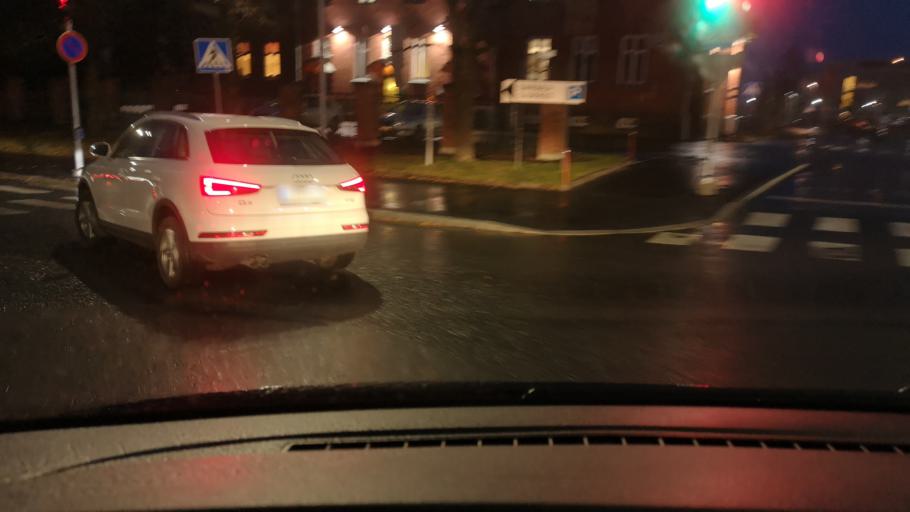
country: FI
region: Ostrobothnia
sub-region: Vaasa
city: Vaasa
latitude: 63.0862
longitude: 21.6142
